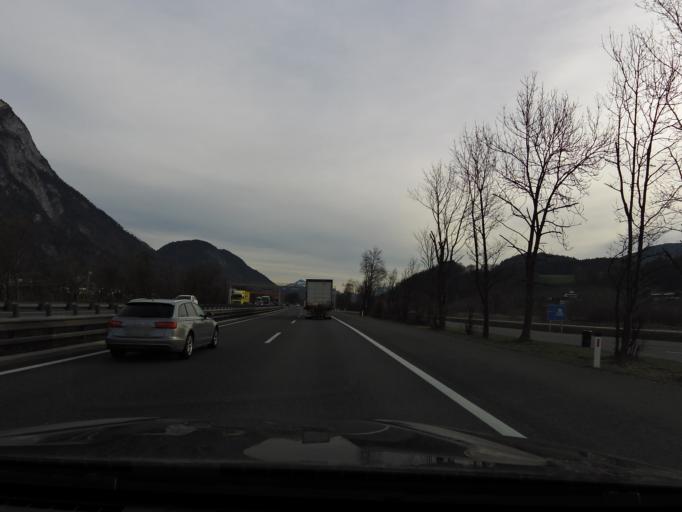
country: AT
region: Tyrol
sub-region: Politischer Bezirk Kufstein
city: Schwoich
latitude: 47.5437
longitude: 12.1165
